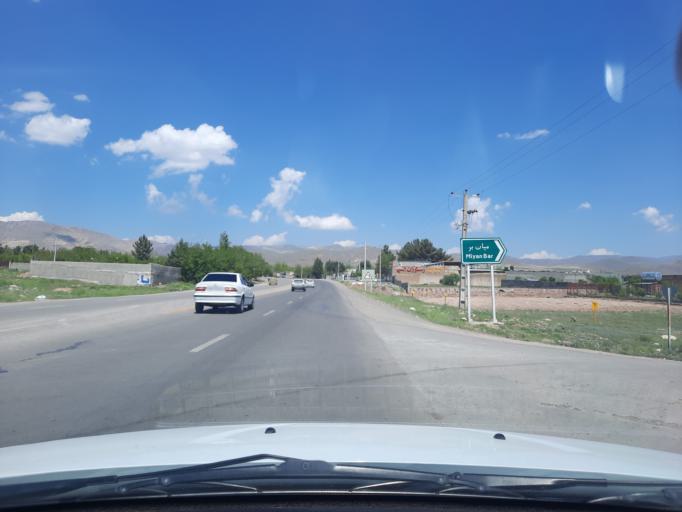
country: IR
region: Qazvin
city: Alvand
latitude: 36.2996
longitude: 50.1420
